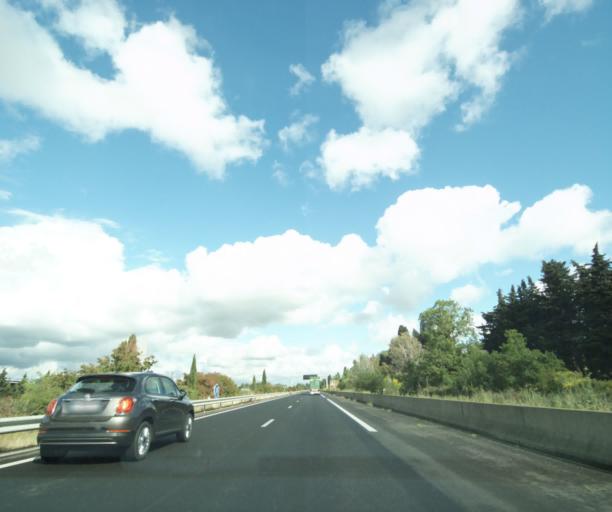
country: FR
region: Provence-Alpes-Cote d'Azur
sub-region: Departement des Bouches-du-Rhone
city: Grans
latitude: 43.6338
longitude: 5.0406
